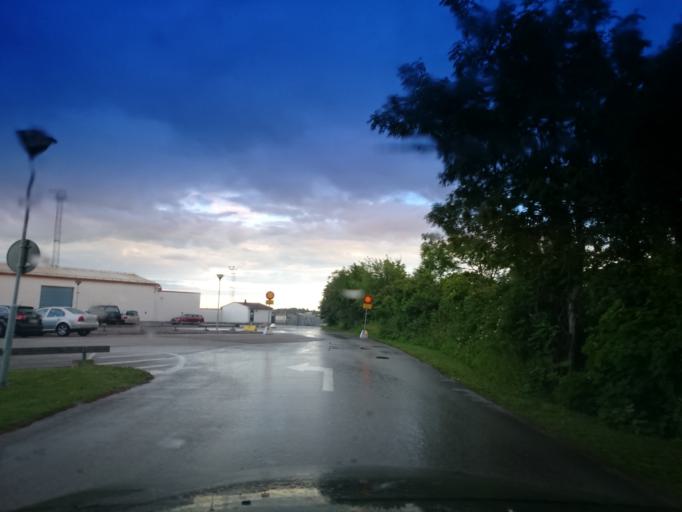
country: SE
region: Gotland
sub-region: Gotland
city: Visby
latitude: 57.6601
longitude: 18.3373
